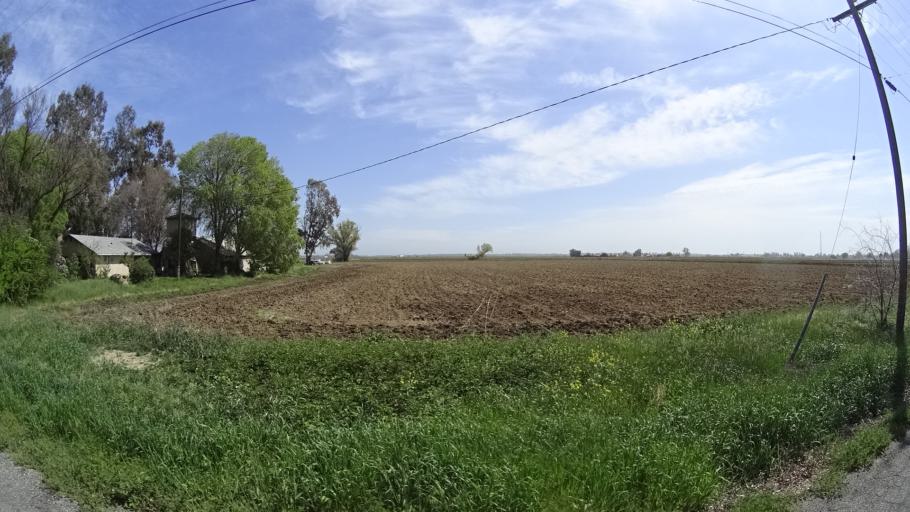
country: US
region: California
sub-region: Glenn County
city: Hamilton City
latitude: 39.6008
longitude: -122.0557
